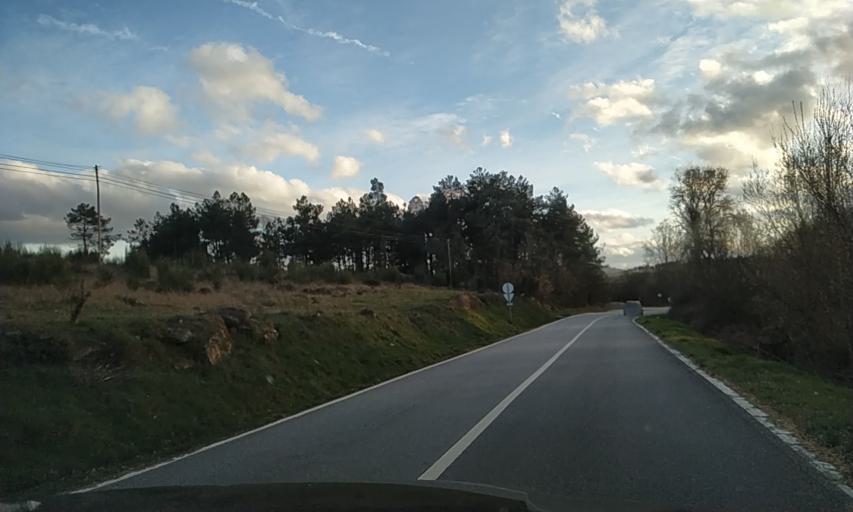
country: PT
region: Braganca
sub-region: Carrazeda de Ansiaes
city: Carrazeda de Anciaes
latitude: 41.2332
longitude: -7.3257
